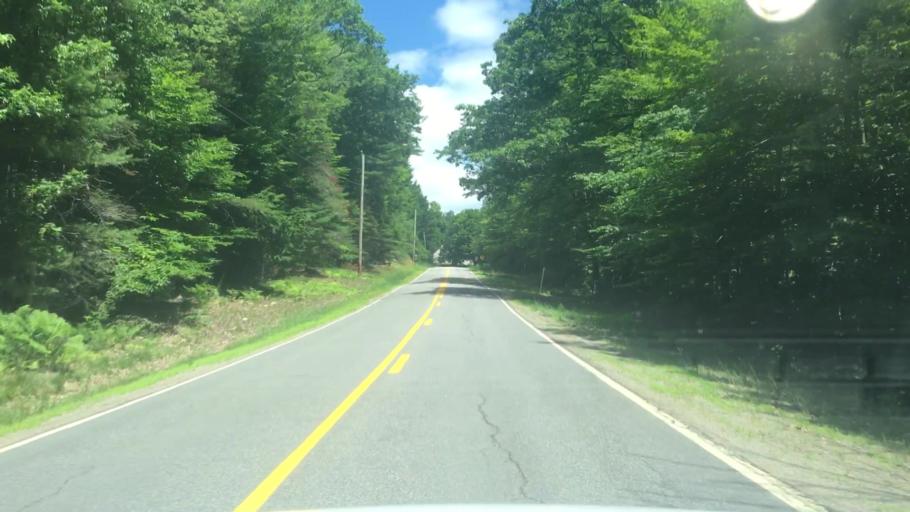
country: US
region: Maine
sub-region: Waldo County
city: Searsmont
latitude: 44.4450
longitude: -69.3058
